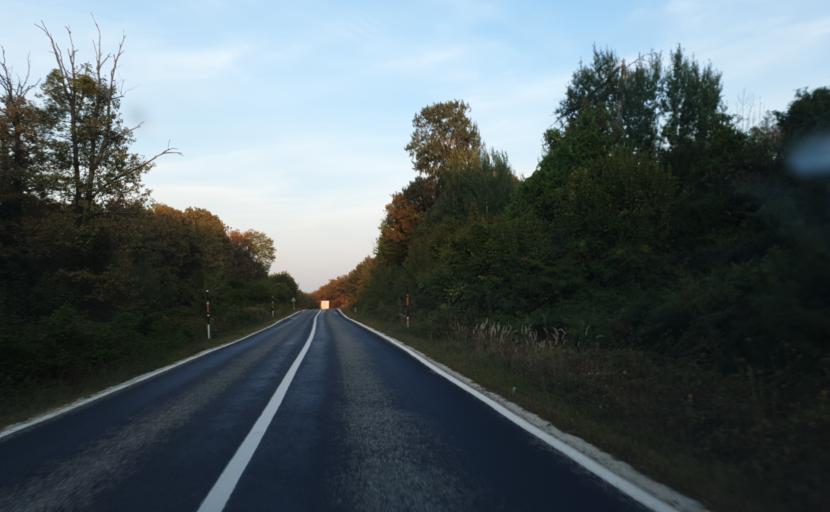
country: TR
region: Kirklareli
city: Igneada
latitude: 41.8609
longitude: 27.8629
